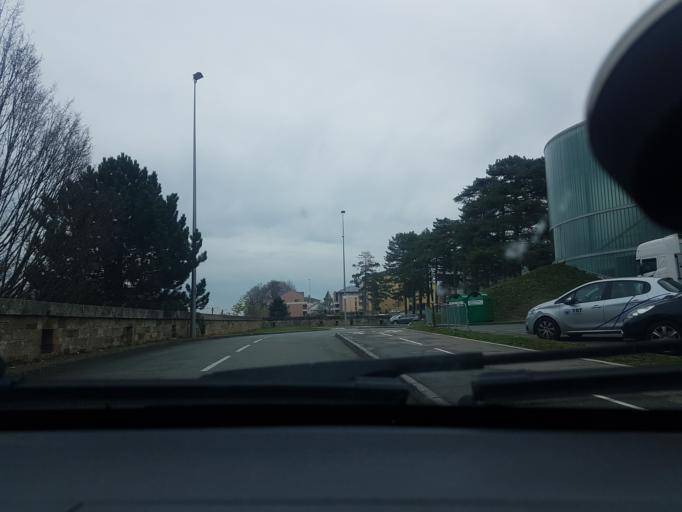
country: FR
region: Franche-Comte
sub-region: Territoire de Belfort
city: Belfort
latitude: 47.6393
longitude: 6.8502
